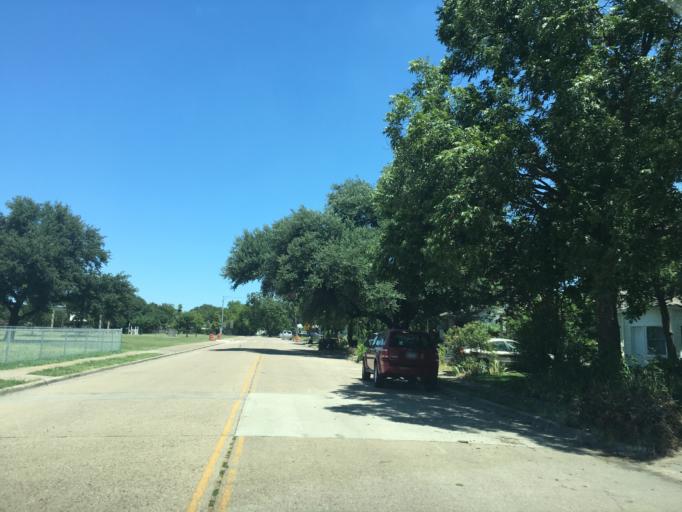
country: US
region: Texas
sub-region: Dallas County
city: Garland
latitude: 32.8452
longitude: -96.6741
